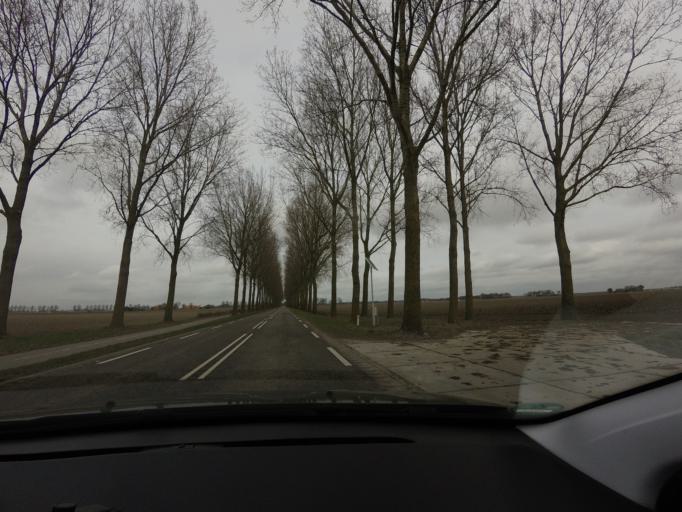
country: NL
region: Friesland
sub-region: Gemeente Lemsterland
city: Lemmer
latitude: 52.7846
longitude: 5.6805
